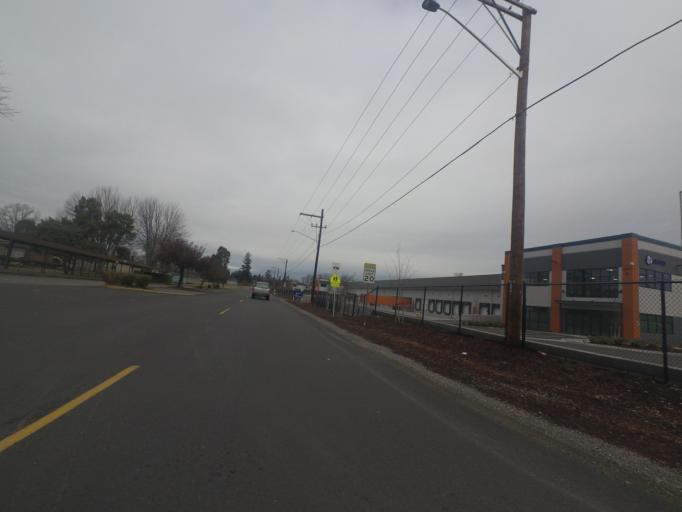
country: US
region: Washington
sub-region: Pierce County
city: Fort Lewis
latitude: 47.1213
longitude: -122.5374
